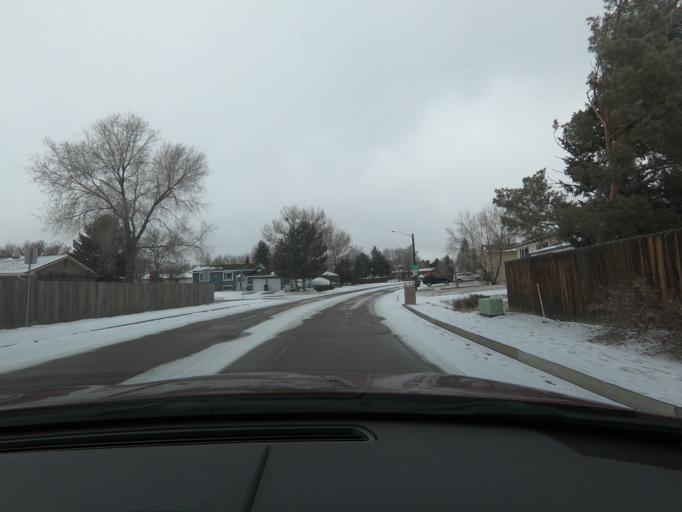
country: US
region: Colorado
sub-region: El Paso County
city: Security-Widefield
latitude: 38.7257
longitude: -104.6927
